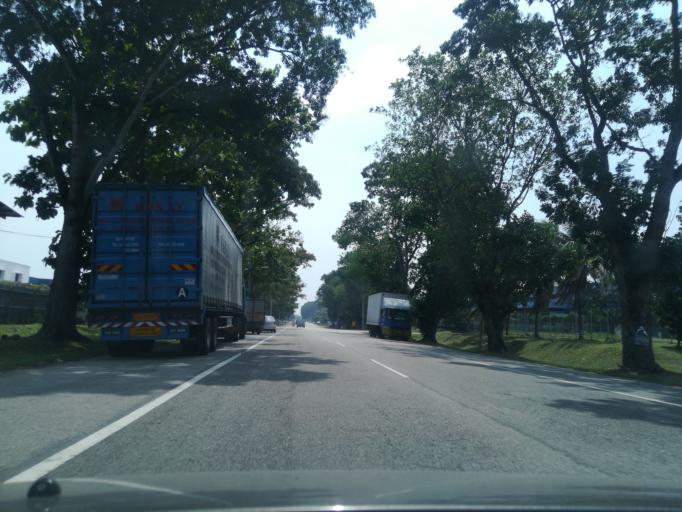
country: MY
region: Kedah
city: Kulim
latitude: 5.4104
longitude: 100.5605
